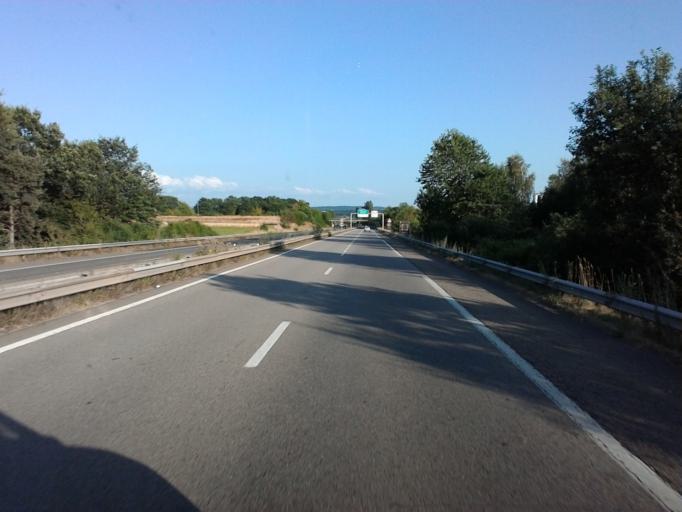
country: FR
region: Lorraine
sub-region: Departement des Vosges
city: Chavelot
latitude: 48.2304
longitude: 6.4256
